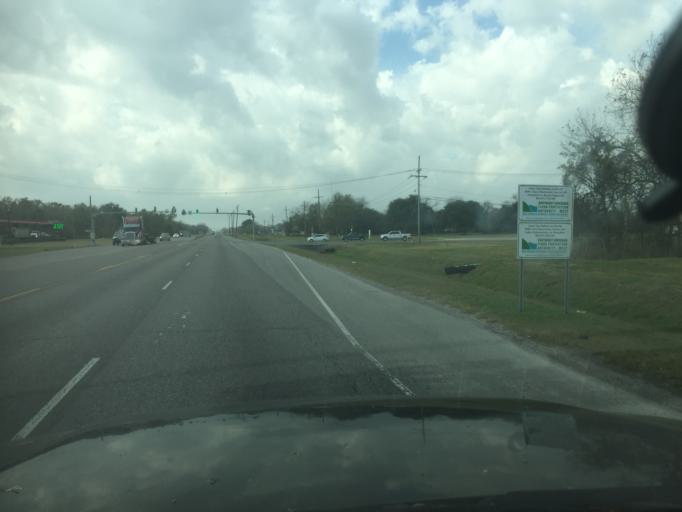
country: US
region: Louisiana
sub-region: Jefferson Parish
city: Avondale
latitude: 29.9105
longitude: -90.2101
